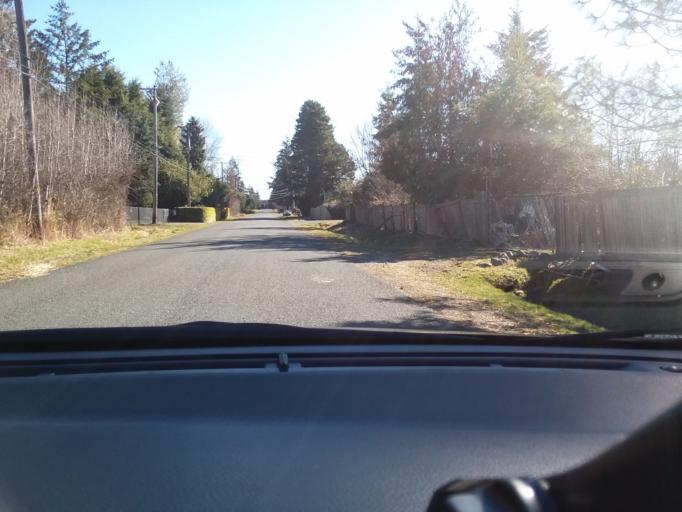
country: US
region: Washington
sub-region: Pierce County
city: Midland
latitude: 47.1725
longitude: -122.4035
